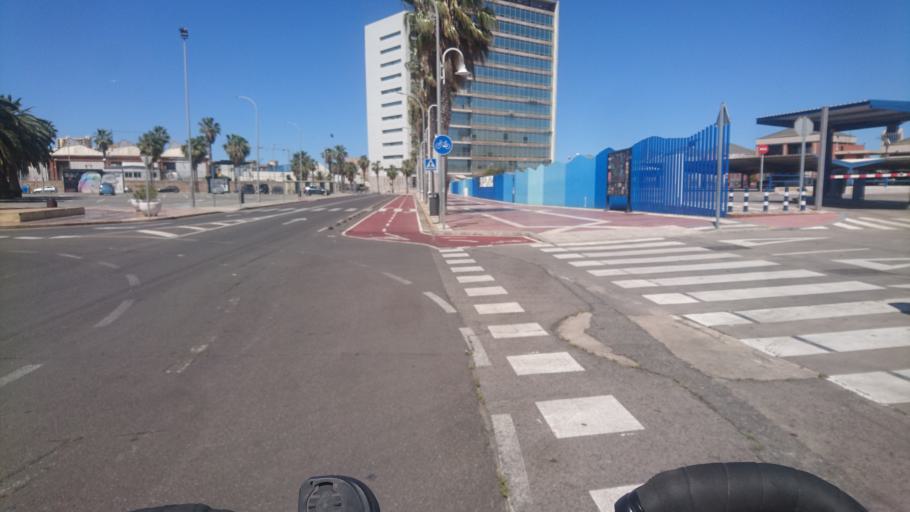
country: ES
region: Melilla
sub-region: Melilla
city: Melilla
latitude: 35.2884
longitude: -2.9371
